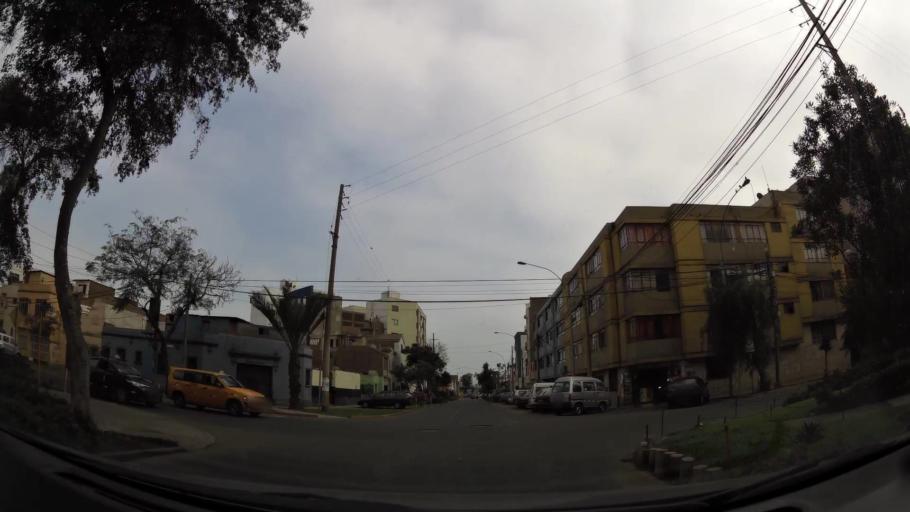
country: PE
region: Lima
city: Lima
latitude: -12.0768
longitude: -77.0495
